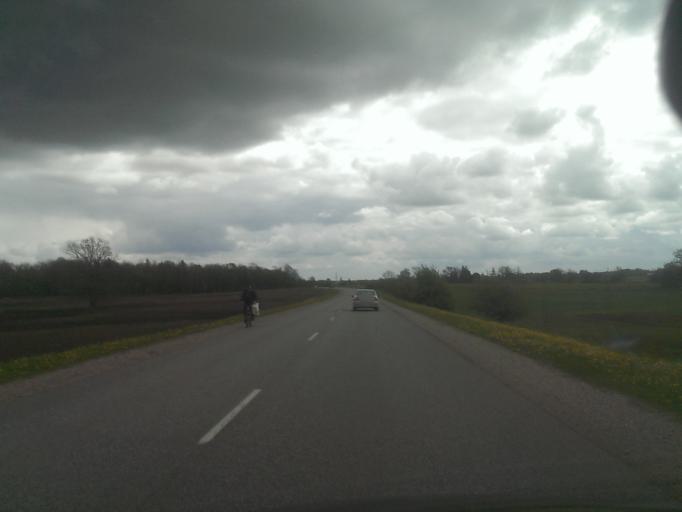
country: LV
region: Kuldigas Rajons
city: Kuldiga
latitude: 56.9891
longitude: 21.9178
